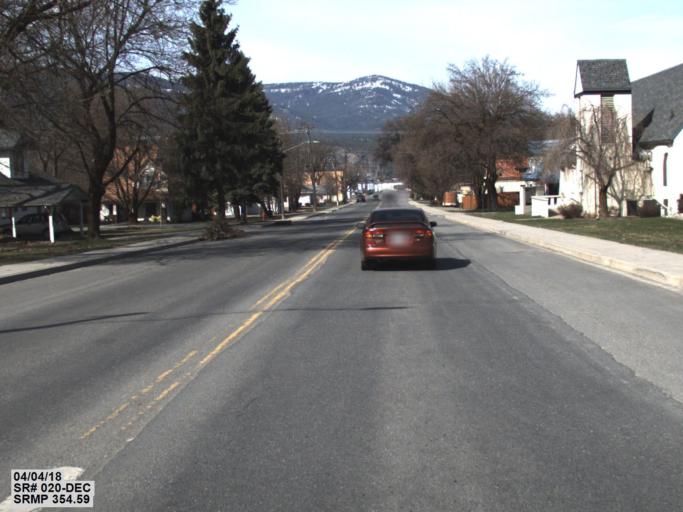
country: US
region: Washington
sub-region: Stevens County
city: Colville
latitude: 48.5466
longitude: -117.9003
